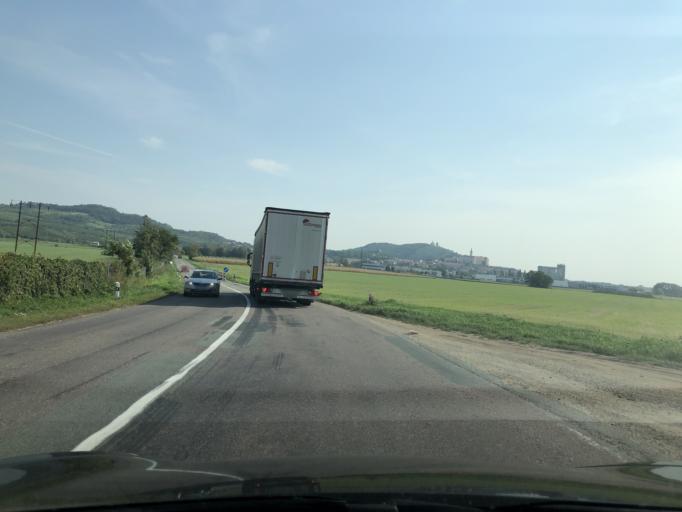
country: CZ
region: South Moravian
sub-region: Okres Breclav
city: Mikulov
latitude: 48.8123
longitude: 16.6087
